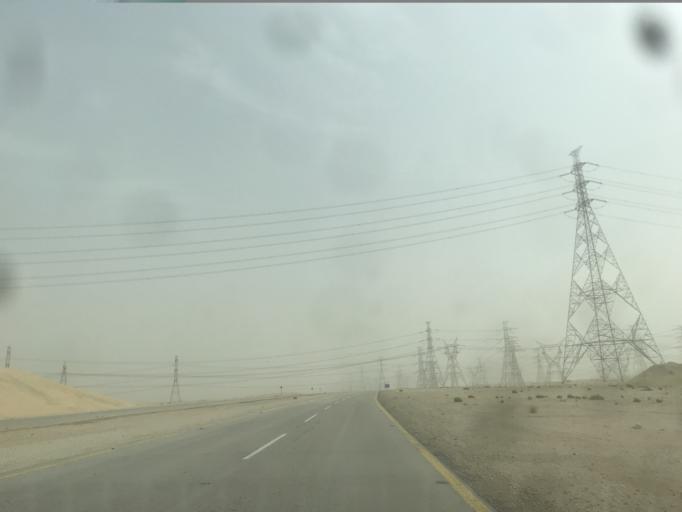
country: SA
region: Eastern Province
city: Abqaiq
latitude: 25.9074
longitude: 49.9035
